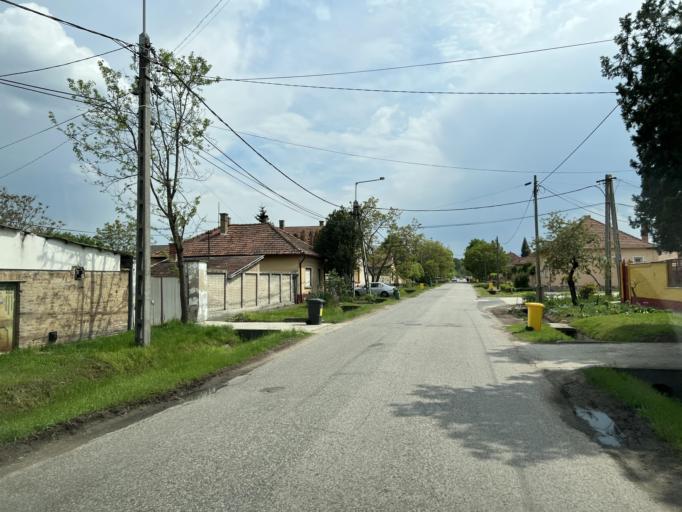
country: HU
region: Pest
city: Nagykoros
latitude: 47.0255
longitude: 19.7878
